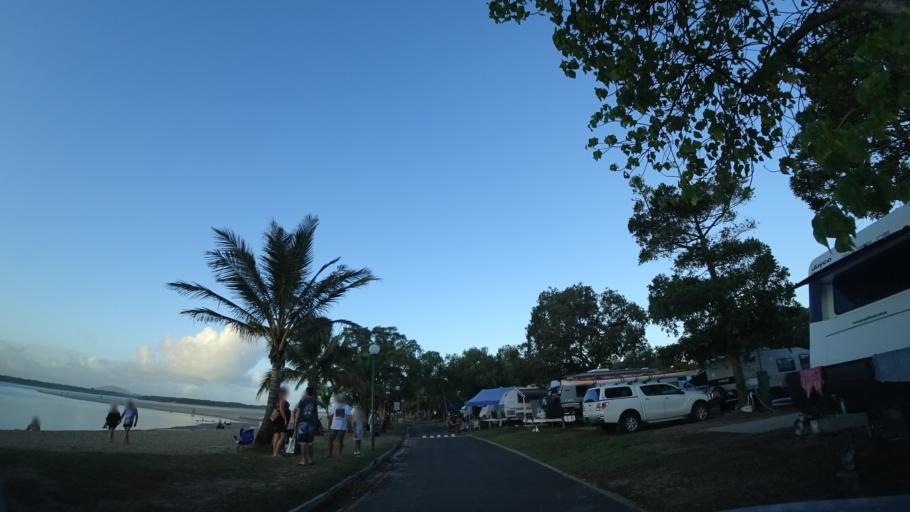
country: AU
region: Queensland
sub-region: Sunshine Coast
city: Mooloolaba
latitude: -26.6527
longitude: 153.0997
